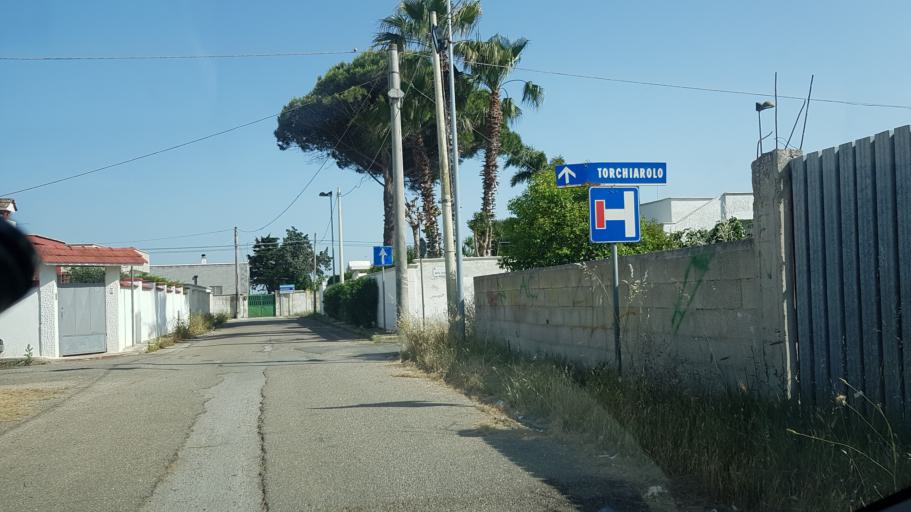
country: IT
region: Apulia
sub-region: Provincia di Brindisi
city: Torchiarolo
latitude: 40.5160
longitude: 18.0821
